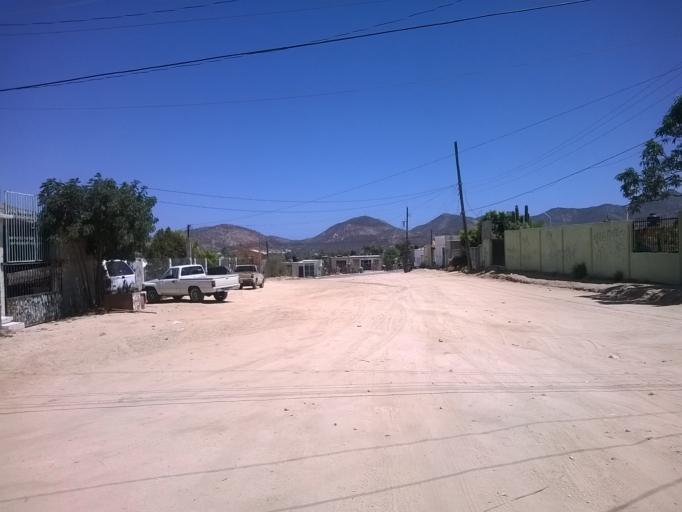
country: MX
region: Baja California Sur
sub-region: Los Cabos
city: Las Veredas
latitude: 23.1435
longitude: -109.7084
